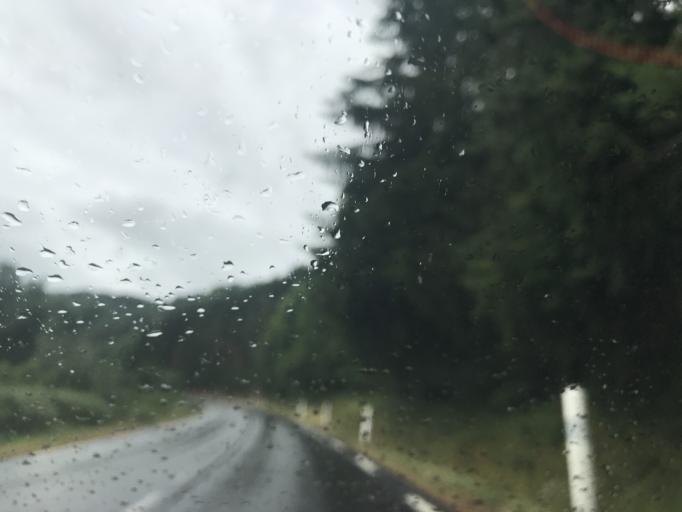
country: FR
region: Auvergne
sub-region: Departement du Puy-de-Dome
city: Job
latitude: 45.5930
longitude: 3.7309
